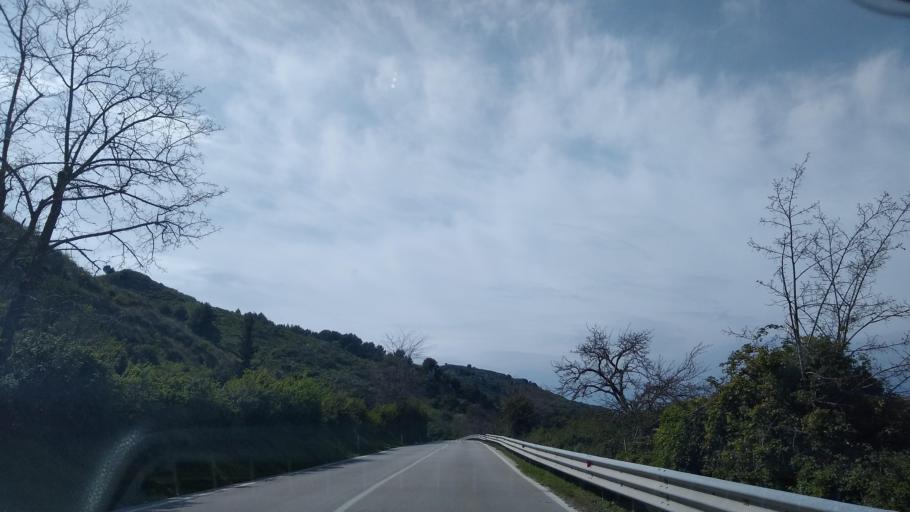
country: IT
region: Sicily
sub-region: Palermo
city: Pioppo
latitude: 38.0374
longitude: 13.2070
